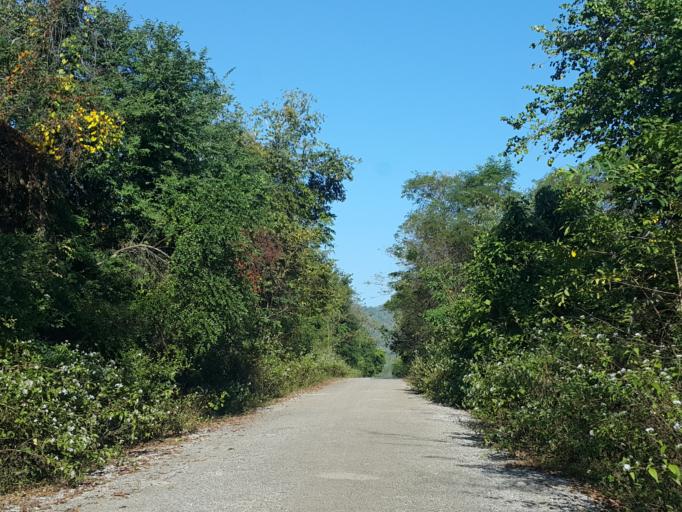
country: TH
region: Lampang
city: Mae Mo
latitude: 18.3023
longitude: 99.6639
